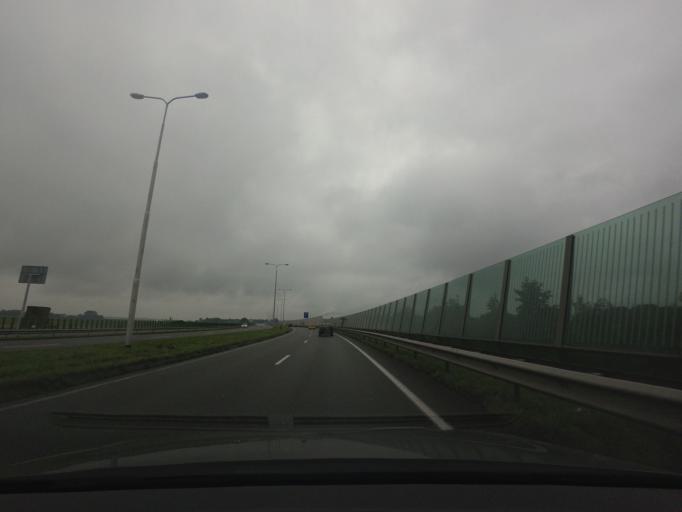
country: NL
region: North Holland
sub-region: Gemeente Alkmaar
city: Alkmaar
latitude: 52.6316
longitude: 4.7832
